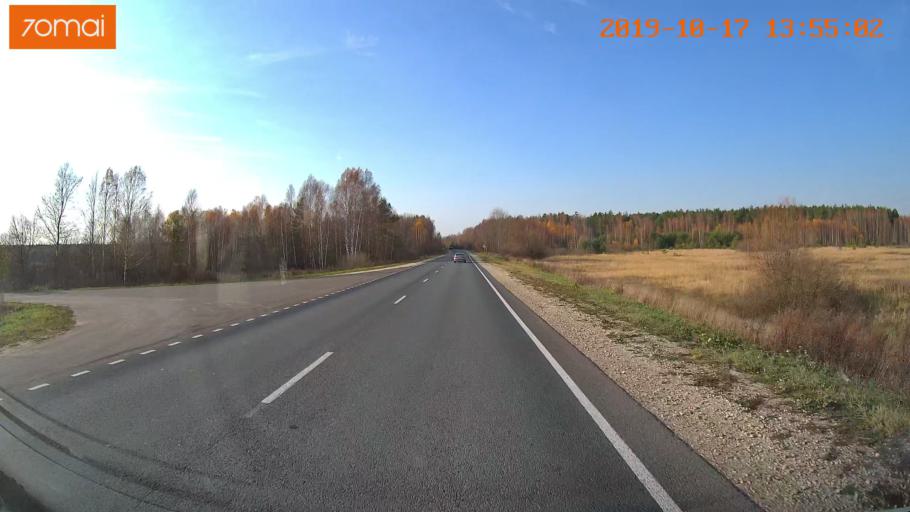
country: RU
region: Rjazan
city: Spas-Klepiki
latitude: 55.1498
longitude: 40.2992
